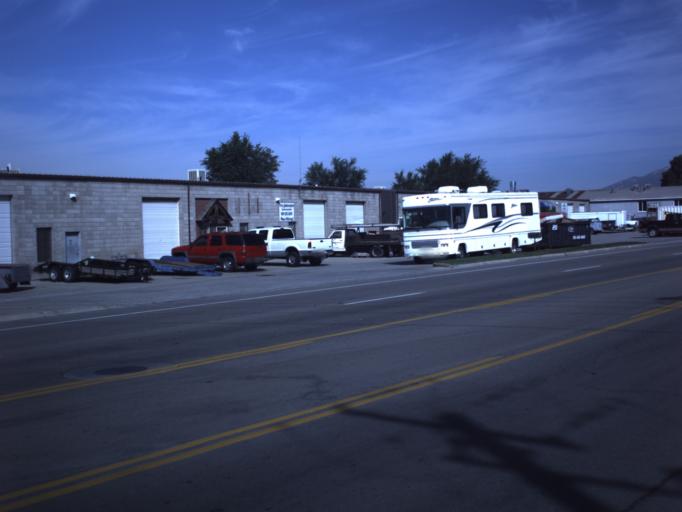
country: US
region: Utah
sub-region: Utah County
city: Pleasant Grove
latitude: 40.3471
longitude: -111.7407
